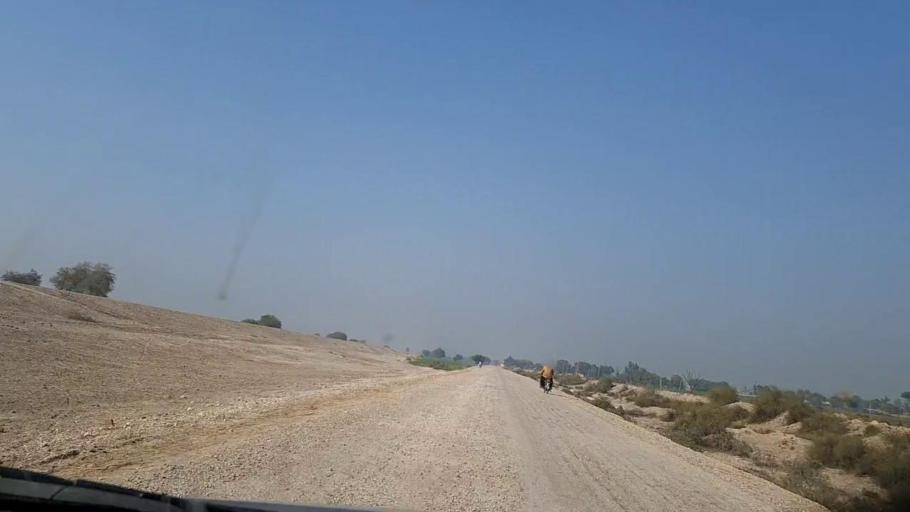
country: PK
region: Sindh
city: Moro
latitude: 26.7256
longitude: 67.9218
